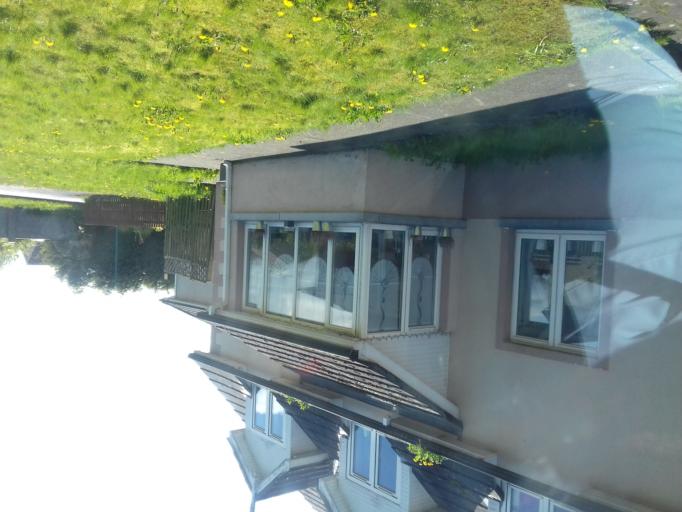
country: IE
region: Leinster
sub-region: Laois
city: Portlaoise
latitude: 53.0449
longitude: -7.2709
